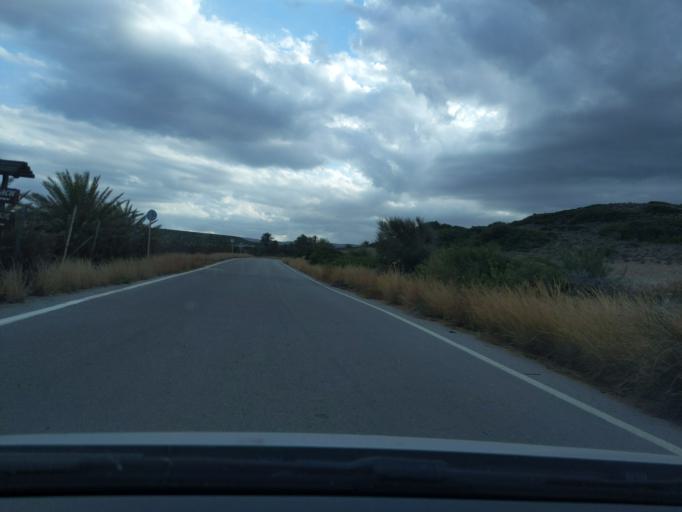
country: GR
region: Crete
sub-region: Nomos Lasithiou
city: Palekastro
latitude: 35.2537
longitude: 26.2531
